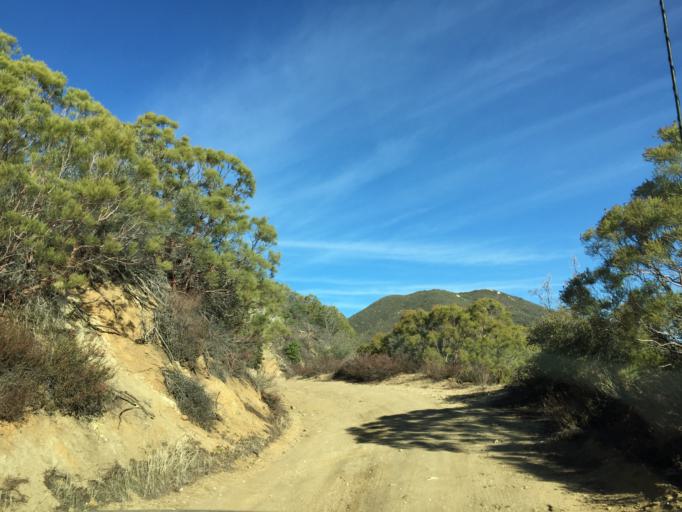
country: US
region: California
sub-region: Riverside County
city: Anza
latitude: 33.5933
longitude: -116.7758
